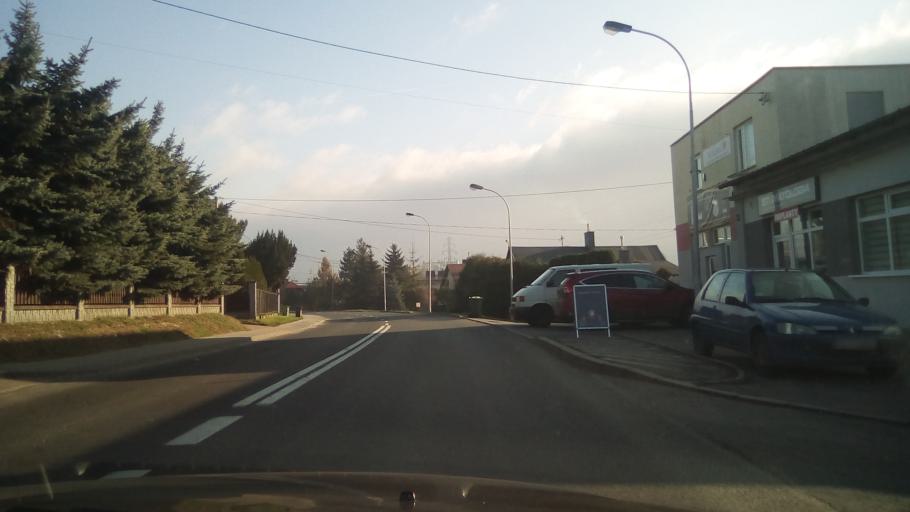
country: PL
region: Subcarpathian Voivodeship
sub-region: Rzeszow
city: Rzeszow
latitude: 50.0537
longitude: 21.9635
